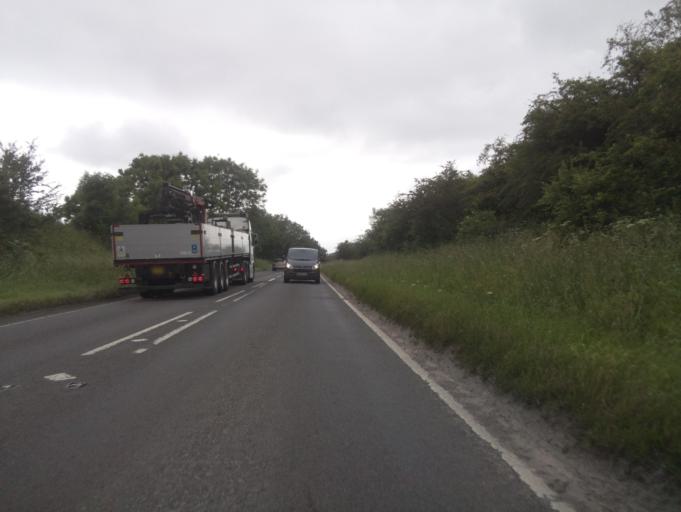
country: GB
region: England
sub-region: Derbyshire
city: Rodsley
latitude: 52.9291
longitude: -1.7633
